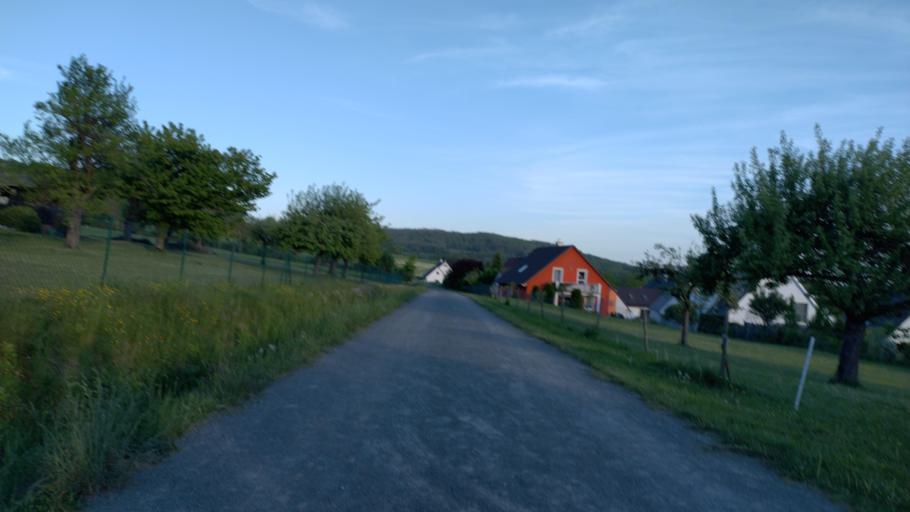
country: DE
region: Bavaria
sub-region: Upper Franconia
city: Bindlach
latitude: 49.9856
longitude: 11.6209
